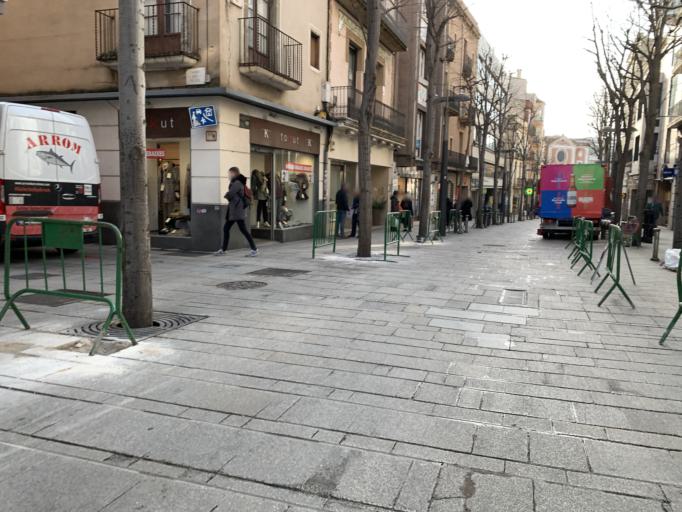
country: ES
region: Catalonia
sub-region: Provincia de Barcelona
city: Mataro
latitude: 41.5393
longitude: 2.4449
